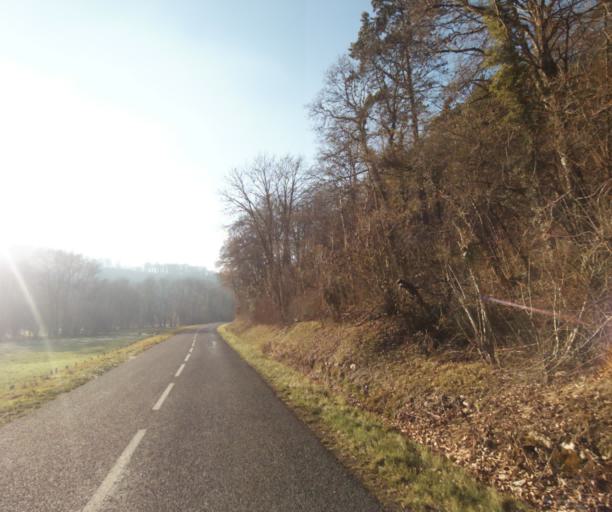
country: FR
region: Champagne-Ardenne
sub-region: Departement de la Haute-Marne
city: Chevillon
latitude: 48.5264
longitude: 5.1662
